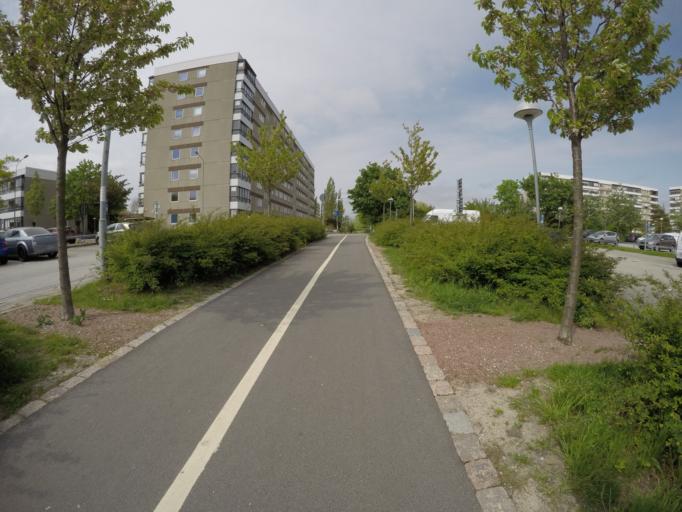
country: SE
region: Skane
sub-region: Malmo
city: Tygelsjo
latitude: 55.5571
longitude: 12.9888
